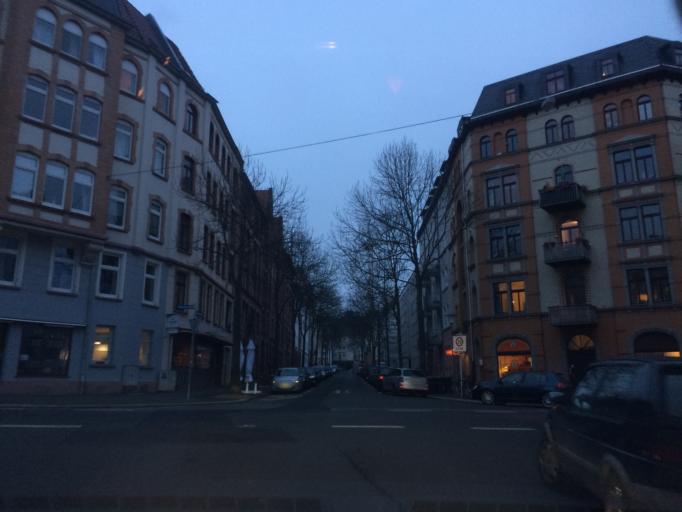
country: DE
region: Hesse
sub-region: Regierungsbezirk Kassel
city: Kassel
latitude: 51.3170
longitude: 9.4665
